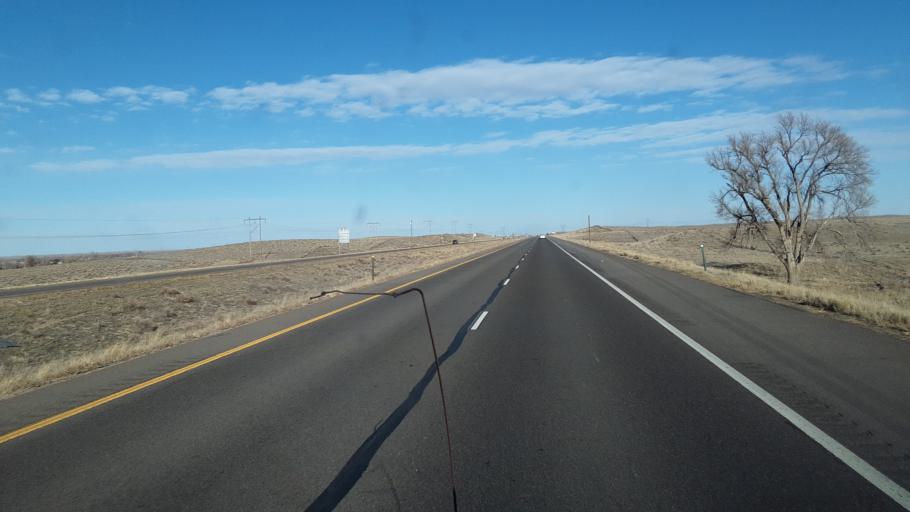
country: US
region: Colorado
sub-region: Morgan County
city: Brush
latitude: 40.2784
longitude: -103.5665
